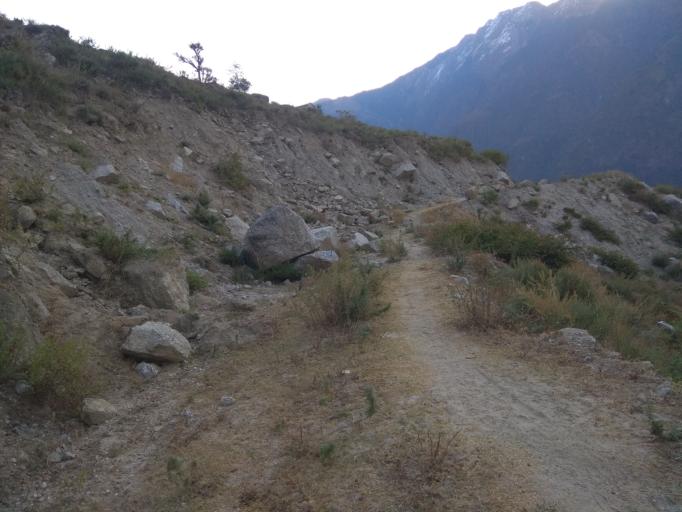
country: NP
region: Far Western
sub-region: Seti Zone
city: Achham
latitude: 29.2313
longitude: 81.6455
